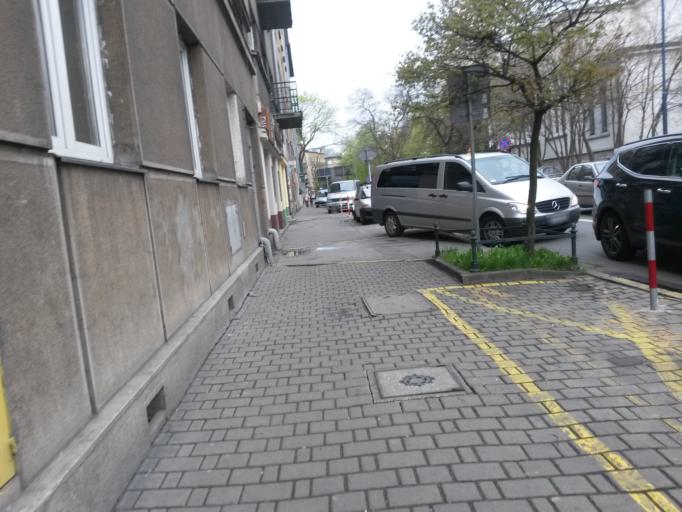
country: PL
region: Lesser Poland Voivodeship
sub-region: Krakow
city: Krakow
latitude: 50.0713
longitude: 19.9279
